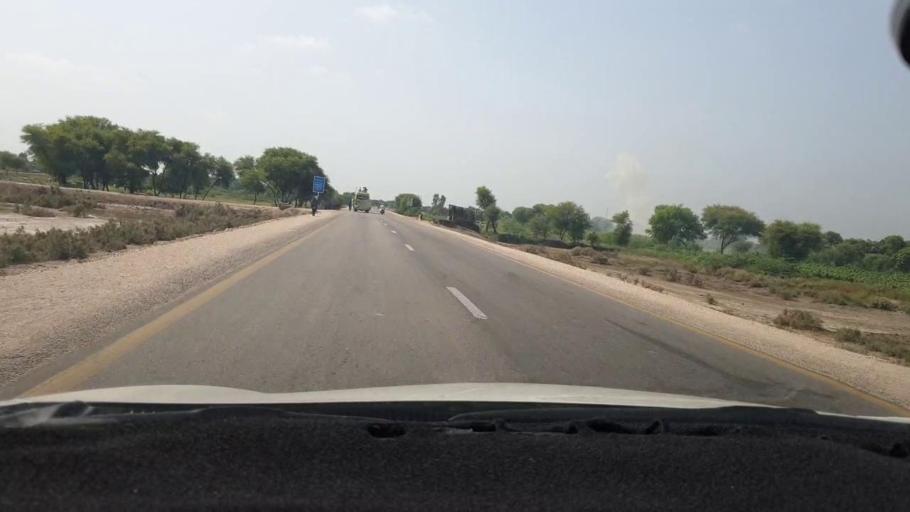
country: PK
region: Sindh
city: Mirpur Khas
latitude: 25.6298
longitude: 69.0919
